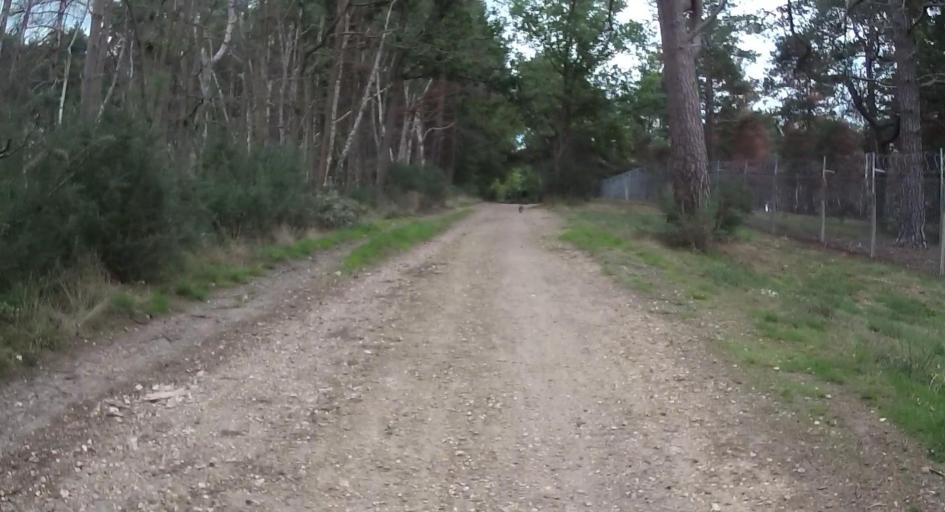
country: GB
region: England
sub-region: Surrey
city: Windlesham
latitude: 51.3431
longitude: -0.6659
